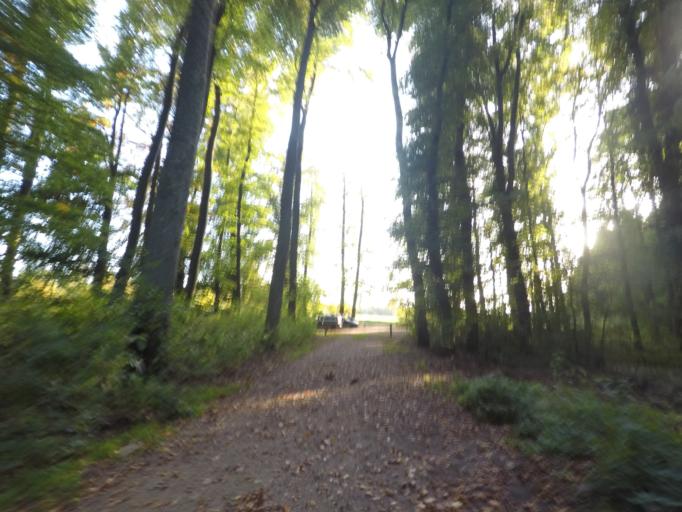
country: LU
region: Luxembourg
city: Itzig
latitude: 49.5936
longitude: 6.1660
